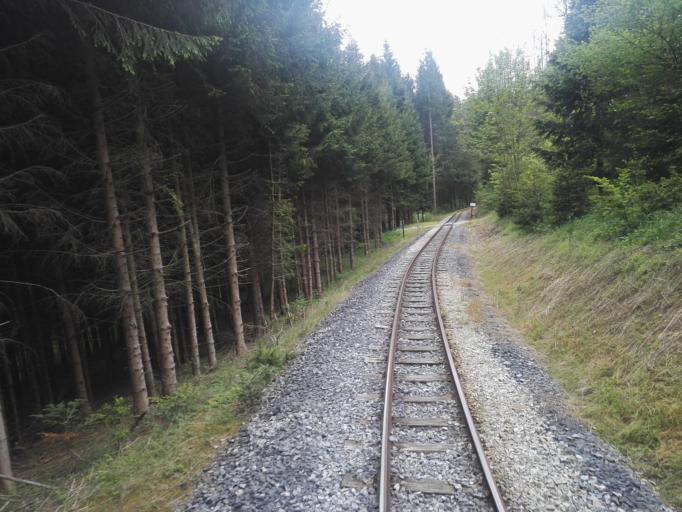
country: AT
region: Styria
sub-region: Politischer Bezirk Weiz
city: Birkfeld
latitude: 47.3463
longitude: 15.6998
